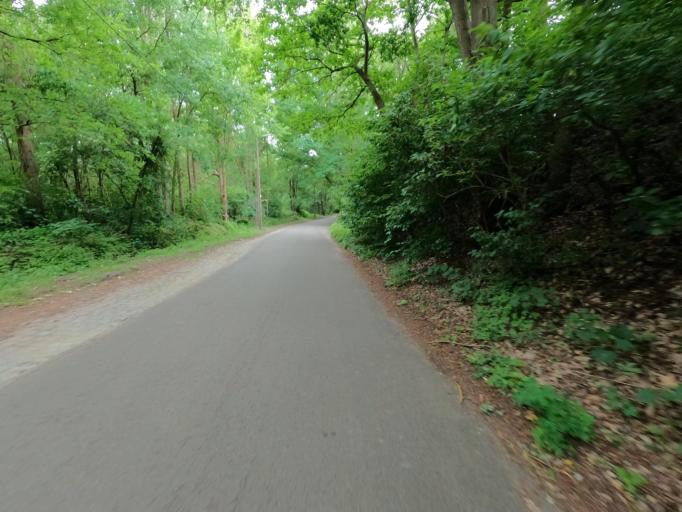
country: BE
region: Flanders
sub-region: Provincie Antwerpen
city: Herentals
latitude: 51.1702
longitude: 4.8075
